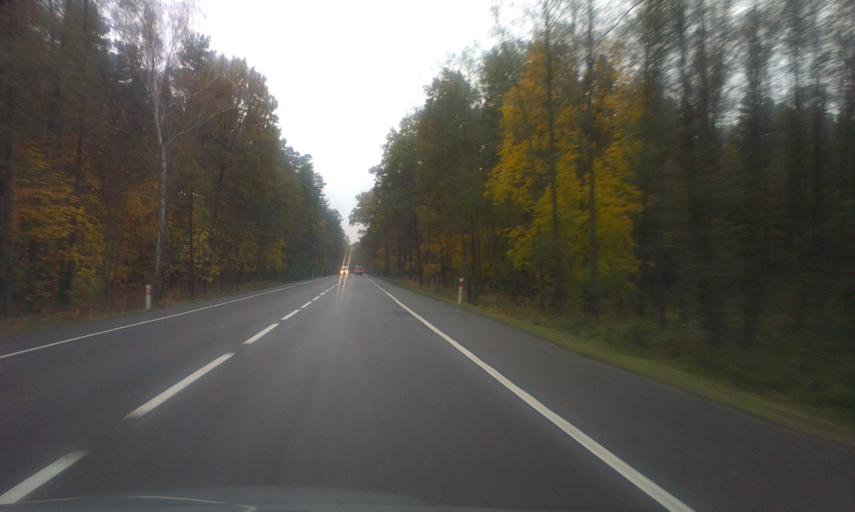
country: PL
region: Greater Poland Voivodeship
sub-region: Powiat chodzieski
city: Budzyn
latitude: 52.8489
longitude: 16.9706
